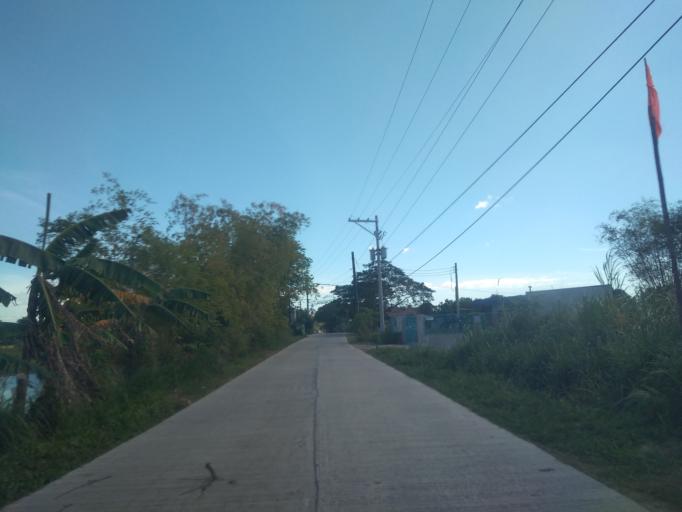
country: PH
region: Central Luzon
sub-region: Province of Pampanga
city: Bacolor
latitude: 15.0165
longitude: 120.6414
